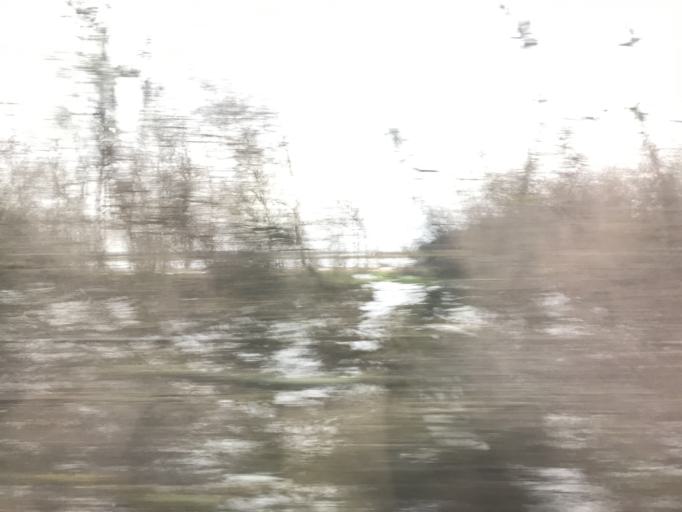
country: AT
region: Burgenland
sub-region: Politischer Bezirk Neusiedl am See
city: Gattendorf
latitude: 47.9861
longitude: 16.9556
